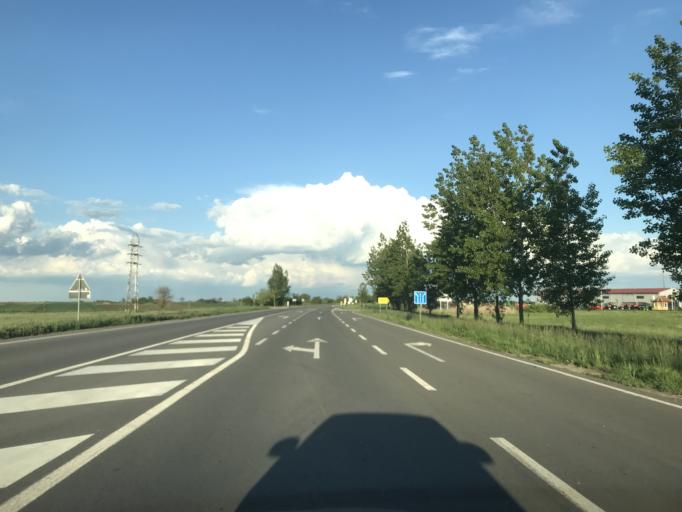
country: RS
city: Aradac
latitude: 45.3922
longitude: 20.2955
